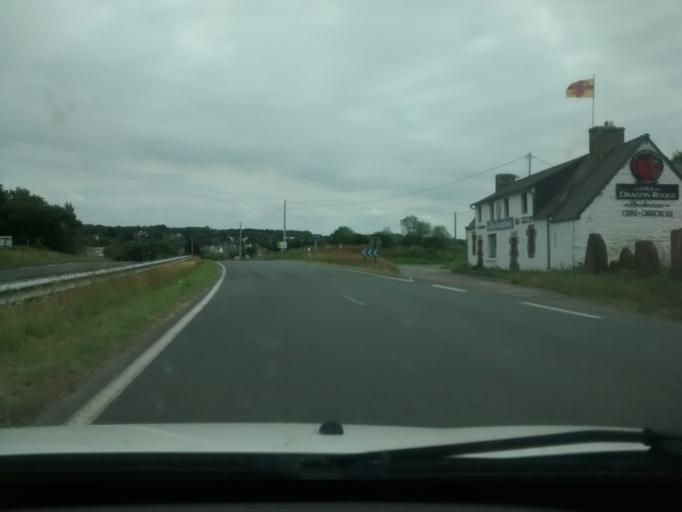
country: FR
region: Brittany
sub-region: Departement des Cotes-d'Armor
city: Saint-Quay-Perros
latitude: 48.7797
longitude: -3.4491
